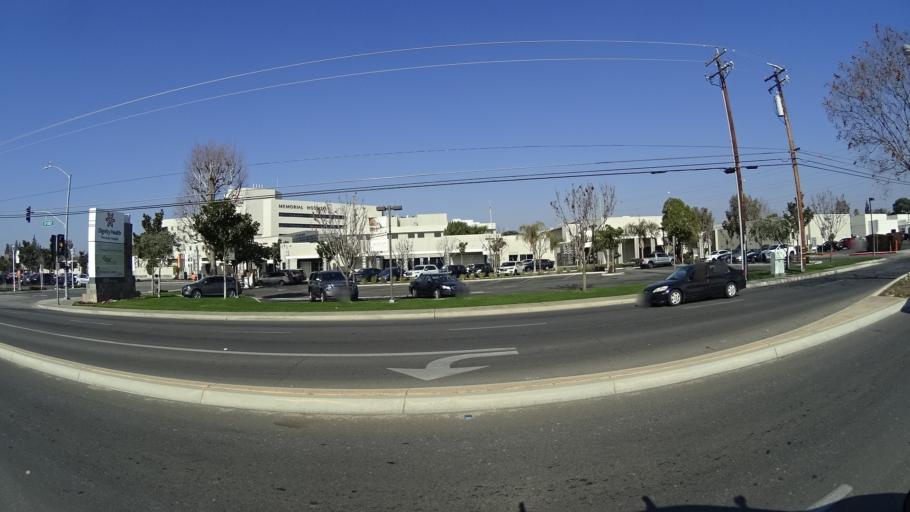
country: US
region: California
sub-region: Kern County
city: Bakersfield
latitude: 35.3904
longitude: -119.0069
